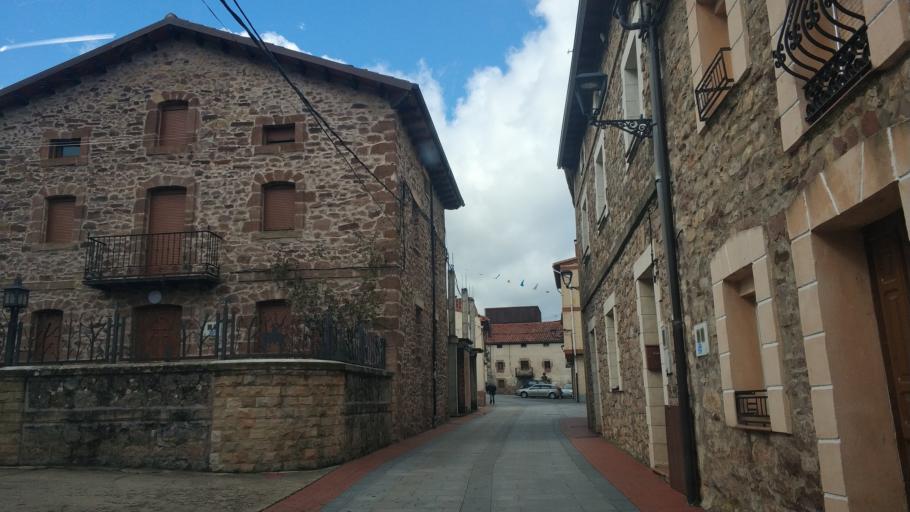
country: ES
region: Castille and Leon
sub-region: Provincia de Burgos
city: Neila
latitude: 42.0604
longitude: -2.9974
